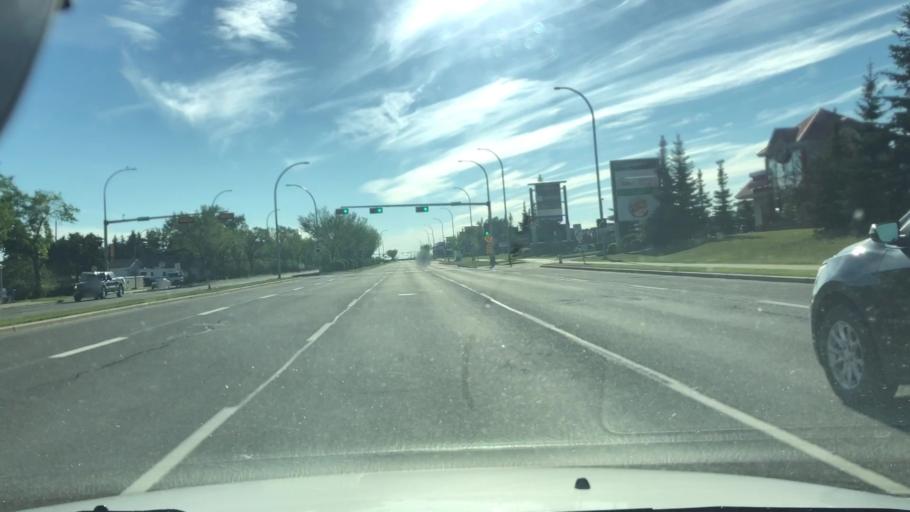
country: CA
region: Alberta
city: St. Albert
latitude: 53.5996
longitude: -113.5522
